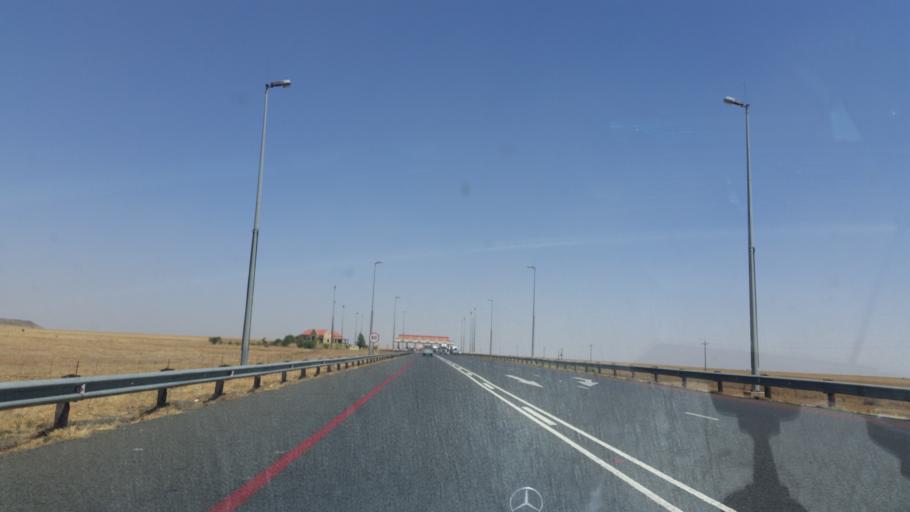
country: ZA
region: Orange Free State
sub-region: Lejweleputswa District Municipality
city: Brandfort
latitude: -28.7959
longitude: 26.6942
